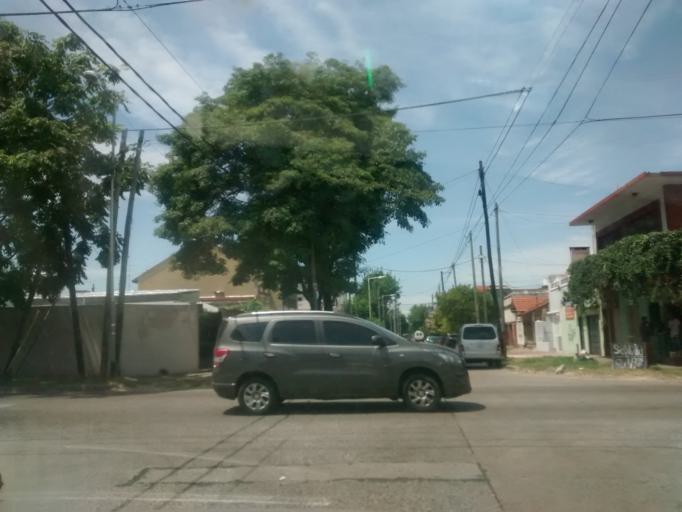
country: AR
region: Buenos Aires
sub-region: Partido de Avellaneda
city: Avellaneda
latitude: -34.6854
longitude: -58.3476
